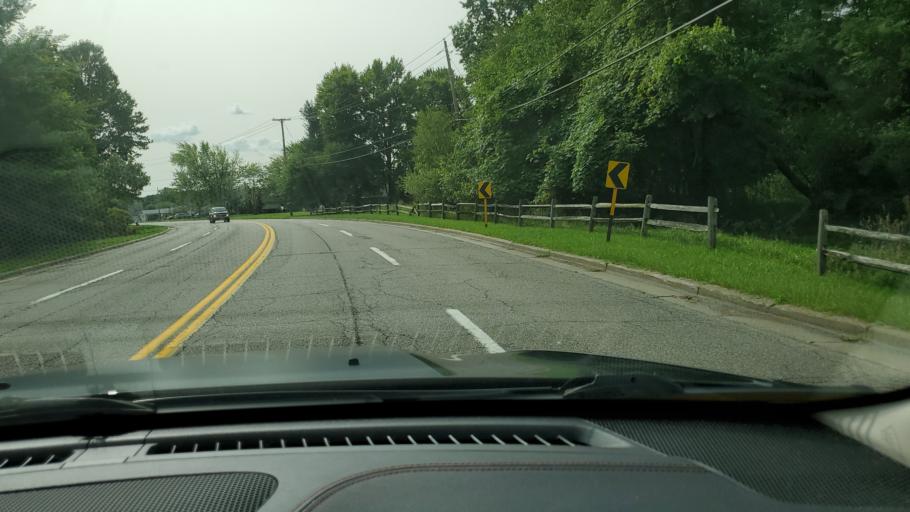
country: US
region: Ohio
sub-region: Mahoning County
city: Boardman
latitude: 40.9928
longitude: -80.6722
